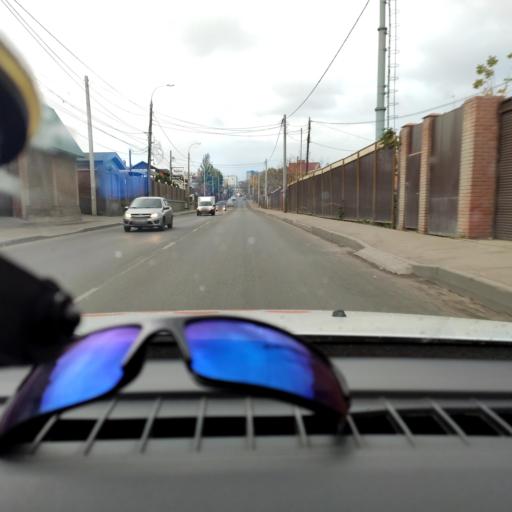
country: RU
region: Samara
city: Samara
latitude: 53.2673
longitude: 50.2015
